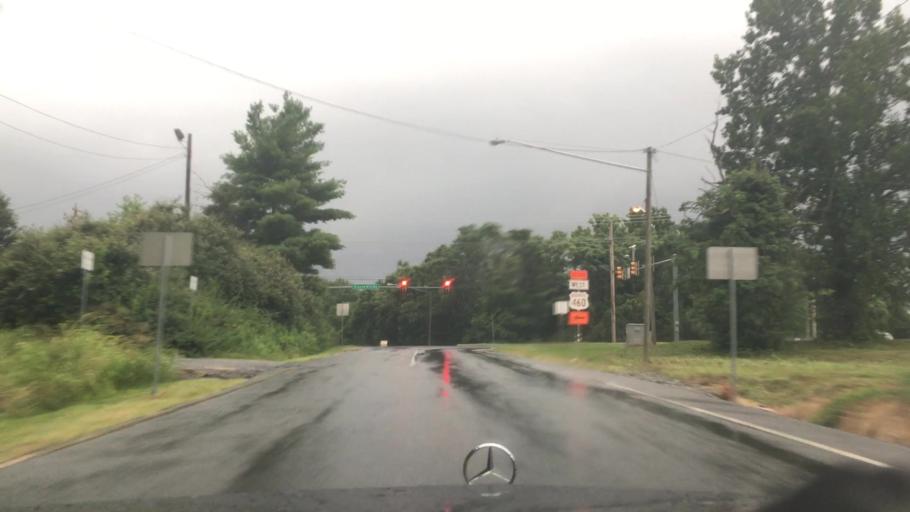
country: US
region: Virginia
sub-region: City of Lynchburg
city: West Lynchburg
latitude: 37.3774
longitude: -79.2220
